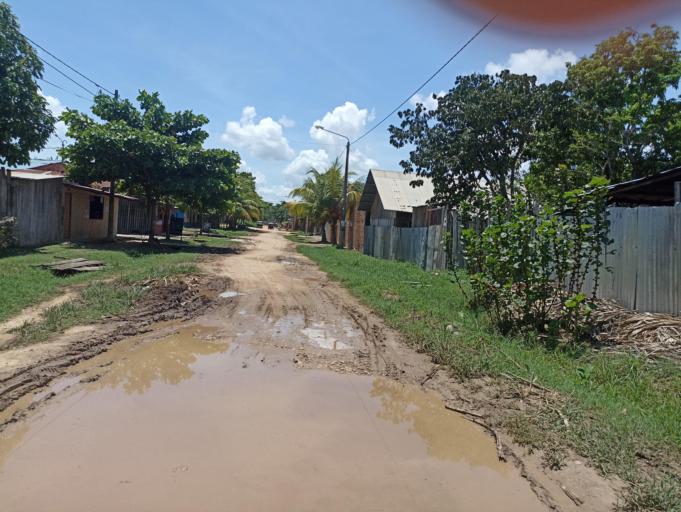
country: PE
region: Ucayali
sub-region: Provincia de Coronel Portillo
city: Puerto Callao
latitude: -8.3611
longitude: -74.5913
